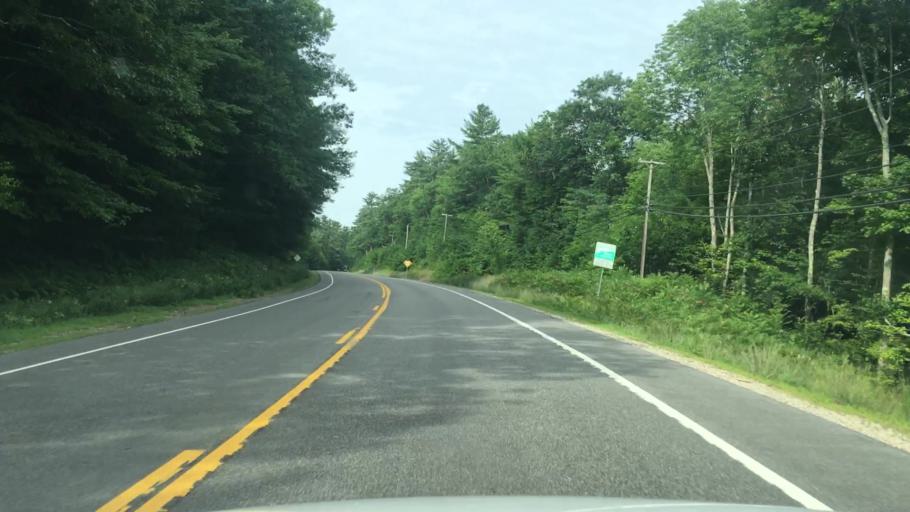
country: US
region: New Hampshire
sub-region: Carroll County
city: Tamworth
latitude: 43.8280
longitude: -71.2960
